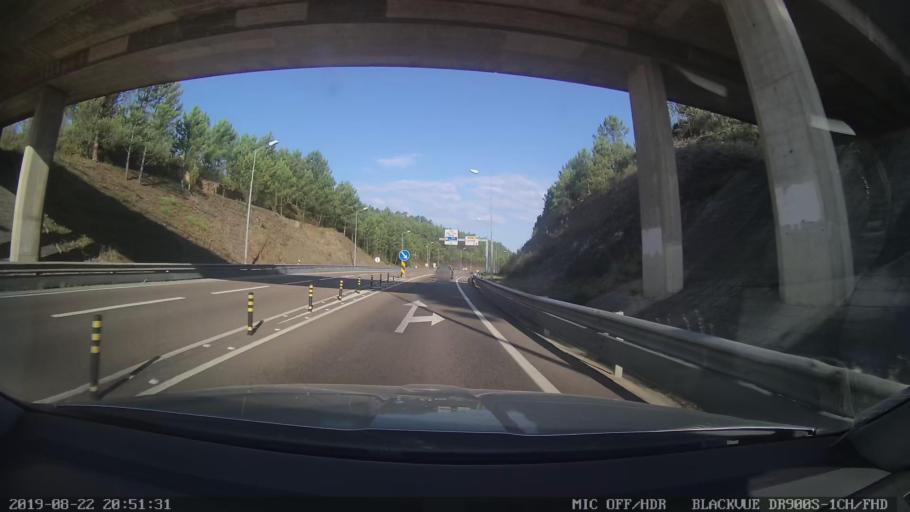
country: PT
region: Castelo Branco
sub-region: Proenca-A-Nova
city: Proenca-a-Nova
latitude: 39.7602
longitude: -7.9612
